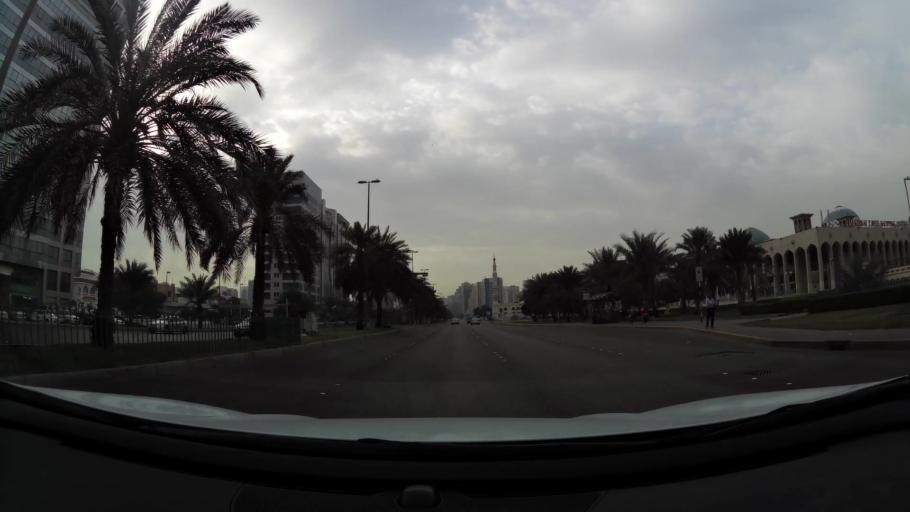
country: AE
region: Abu Dhabi
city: Abu Dhabi
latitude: 24.4856
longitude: 54.3658
